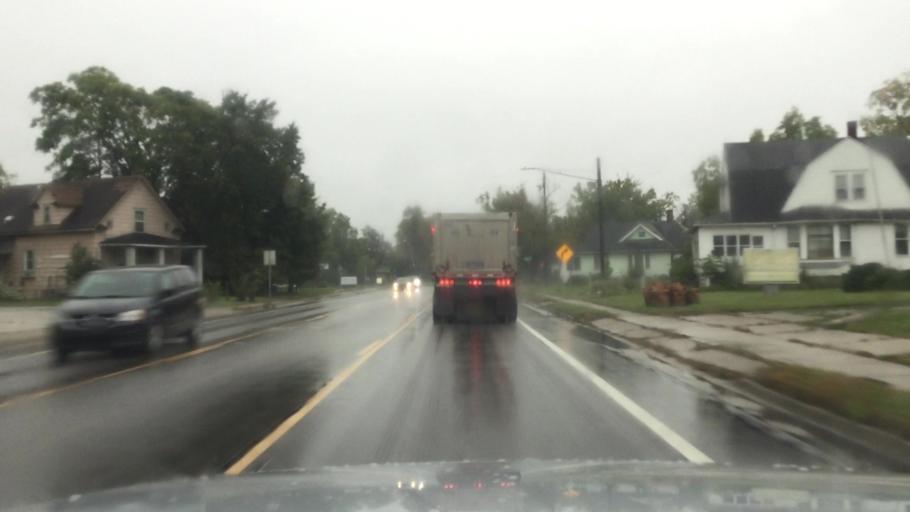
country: US
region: Michigan
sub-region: Saginaw County
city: Saginaw
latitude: 43.3986
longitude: -83.9577
